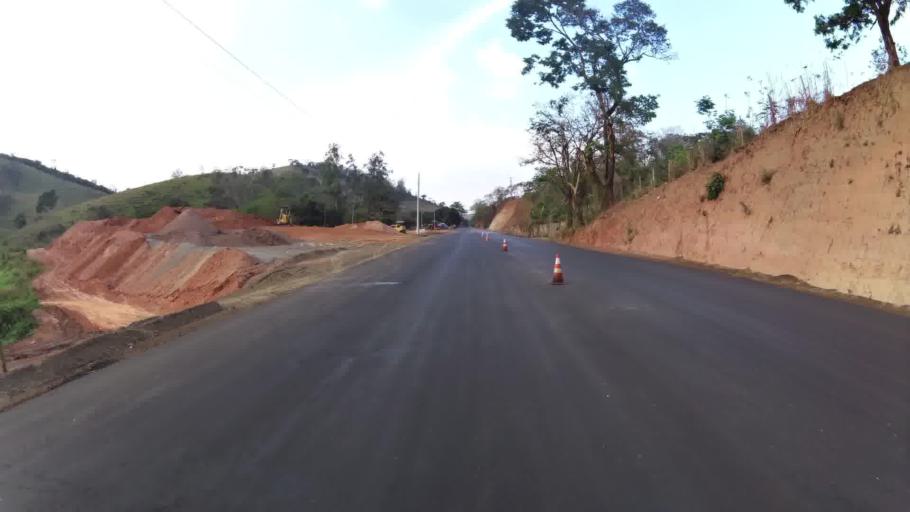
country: BR
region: Rio de Janeiro
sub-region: Santo Antonio De Padua
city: Santo Antonio de Padua
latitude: -21.5057
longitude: -42.0829
